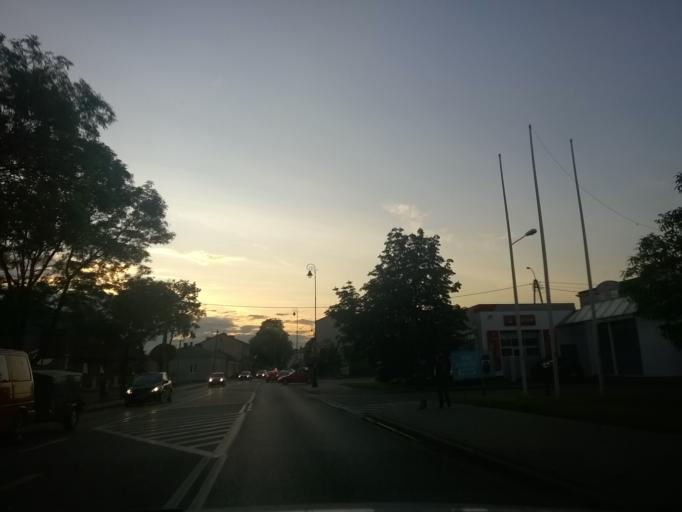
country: PL
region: Masovian Voivodeship
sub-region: Powiat piaseczynski
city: Konstancin-Jeziorna
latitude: 52.0920
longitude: 21.1194
